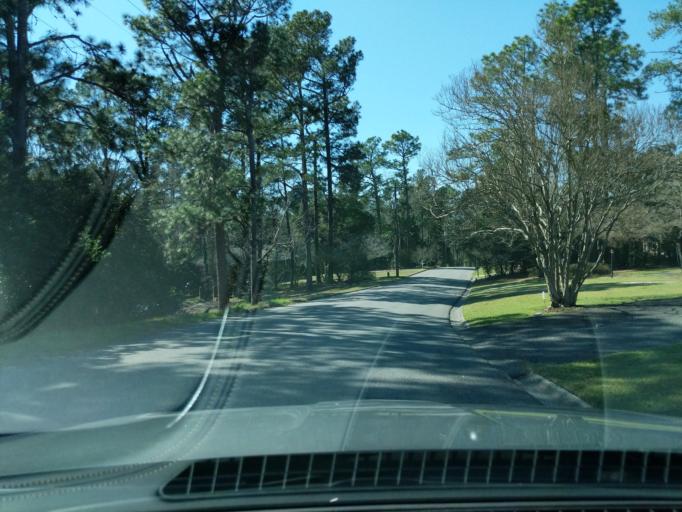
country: US
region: South Carolina
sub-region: Aiken County
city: Aiken
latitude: 33.5326
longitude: -81.7398
